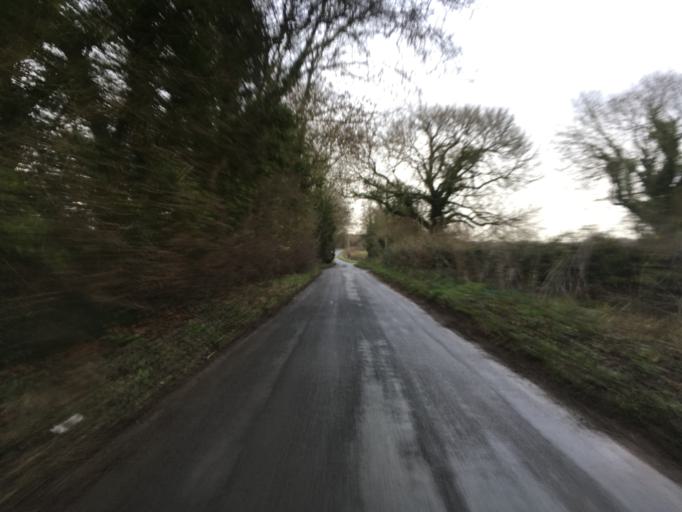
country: GB
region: England
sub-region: Wiltshire
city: Nettleton
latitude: 51.5082
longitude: -2.2929
